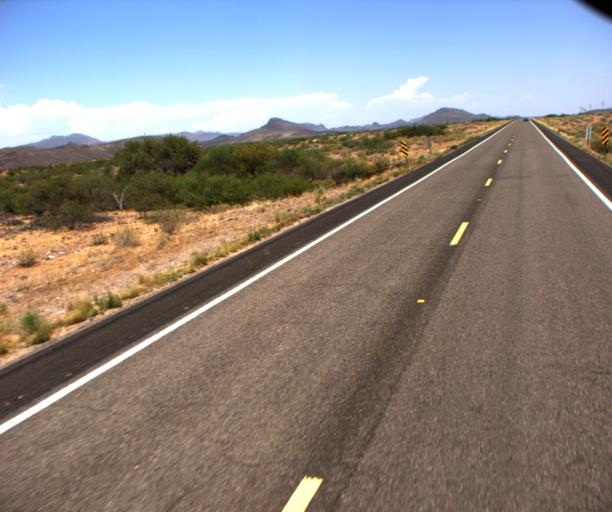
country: US
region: Arizona
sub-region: Graham County
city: Cactus Flat
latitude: 32.7682
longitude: -109.4698
